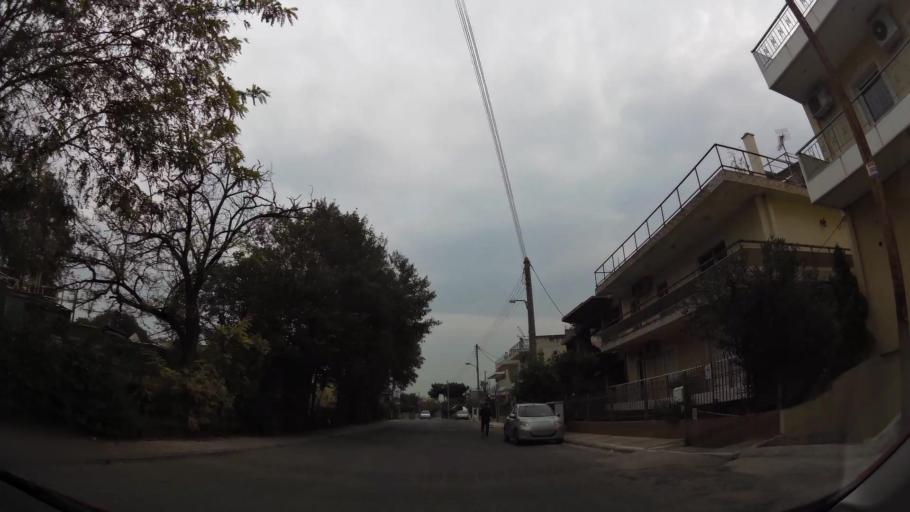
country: GR
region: Attica
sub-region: Nomarchia Athinas
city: Ilion
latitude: 38.0400
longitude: 23.7096
